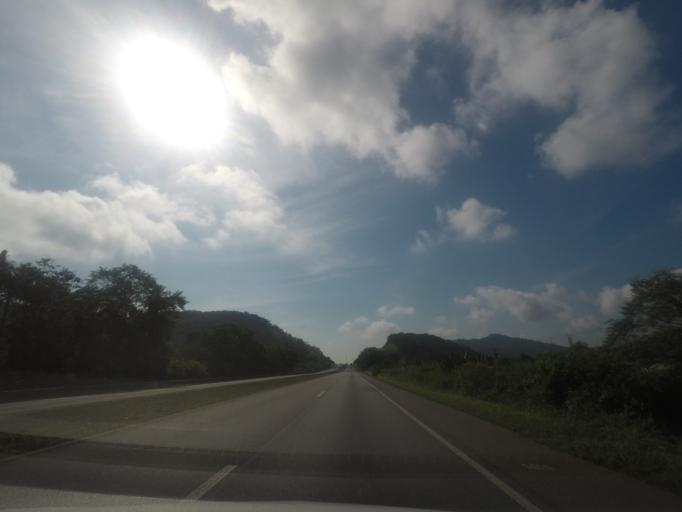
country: BR
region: Parana
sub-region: Antonina
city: Antonina
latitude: -25.5356
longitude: -48.7630
